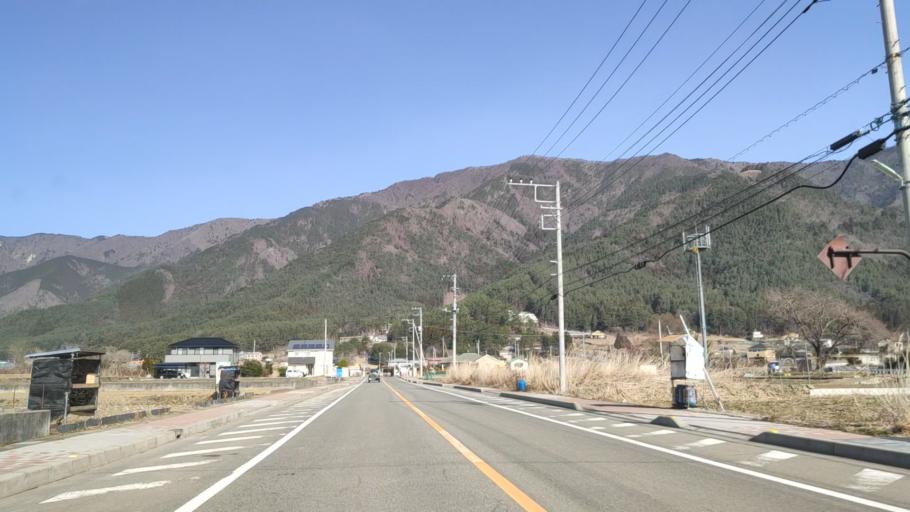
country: JP
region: Yamanashi
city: Fujikawaguchiko
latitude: 35.5218
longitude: 138.7395
